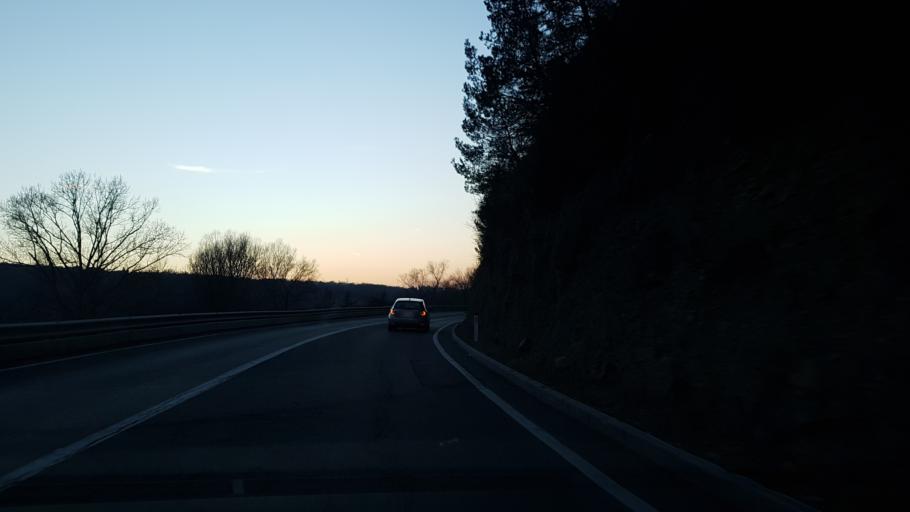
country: SI
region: Koper-Capodistria
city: Dekani
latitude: 45.5438
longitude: 13.8221
